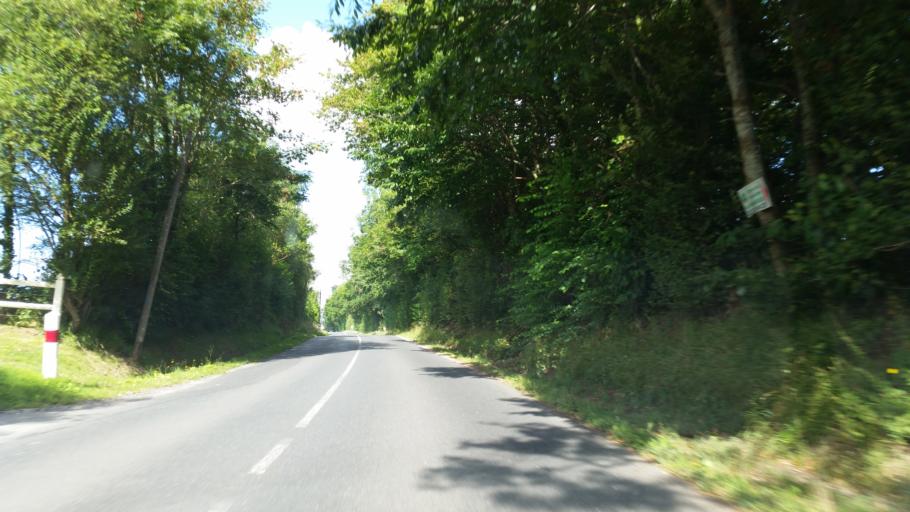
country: FR
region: Lower Normandy
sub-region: Departement du Calvados
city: Dozule
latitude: 49.2583
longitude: -0.0522
